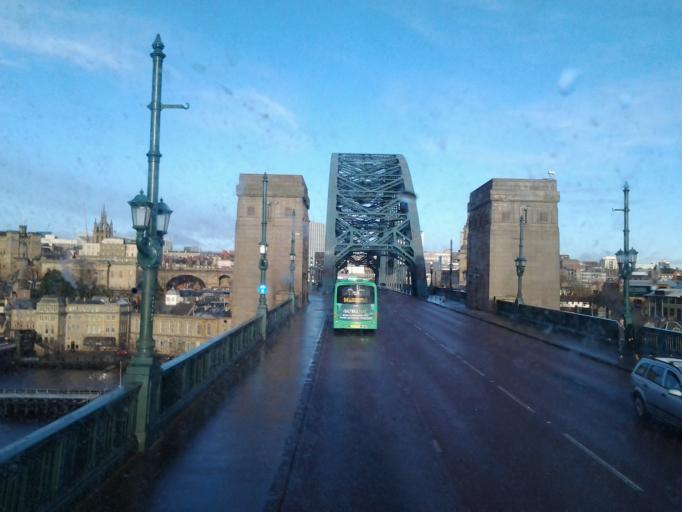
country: GB
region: England
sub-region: Gateshead
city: Gateshead
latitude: 54.9667
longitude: -1.6048
